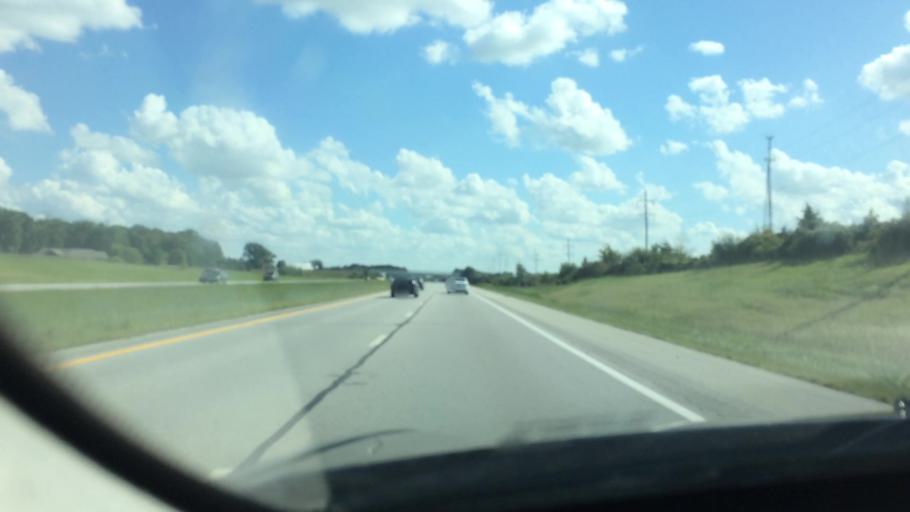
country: US
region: Ohio
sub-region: Shelby County
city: Anna
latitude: 40.3513
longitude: -84.1602
